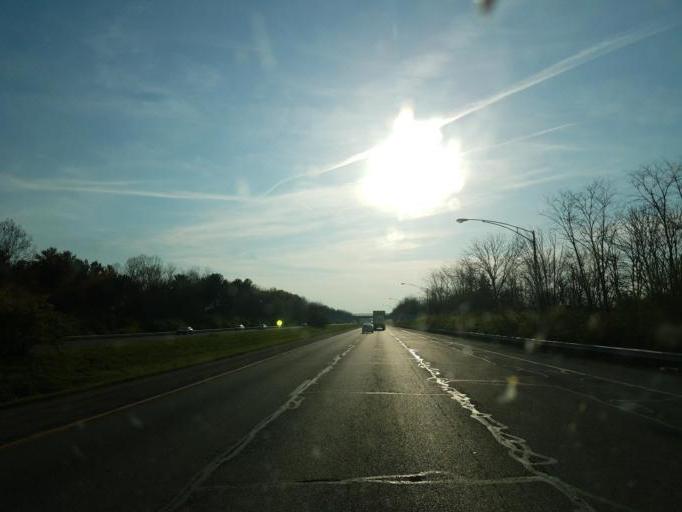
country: US
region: Ohio
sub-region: Warren County
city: Morrow
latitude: 39.4148
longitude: -84.1272
